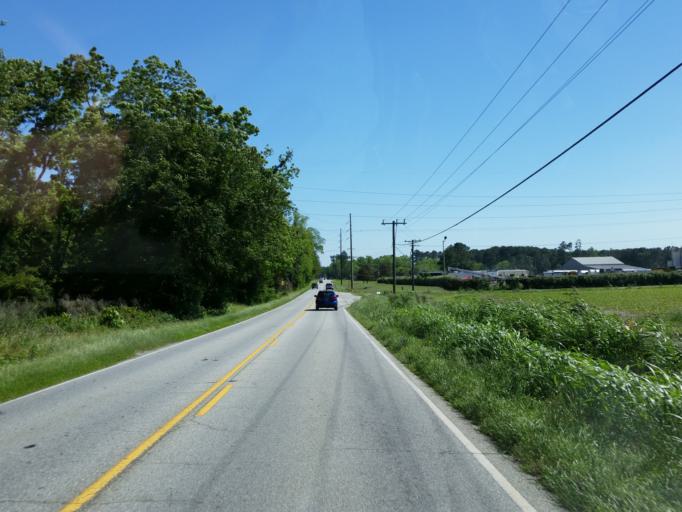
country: US
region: Georgia
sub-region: Lowndes County
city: Hahira
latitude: 30.9354
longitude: -83.3498
